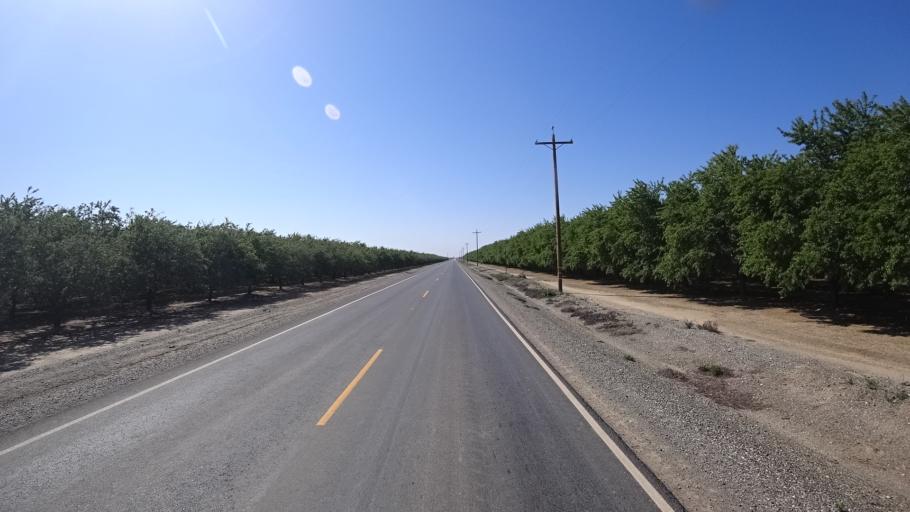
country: US
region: California
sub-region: Glenn County
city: Hamilton City
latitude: 39.6571
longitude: -122.0651
